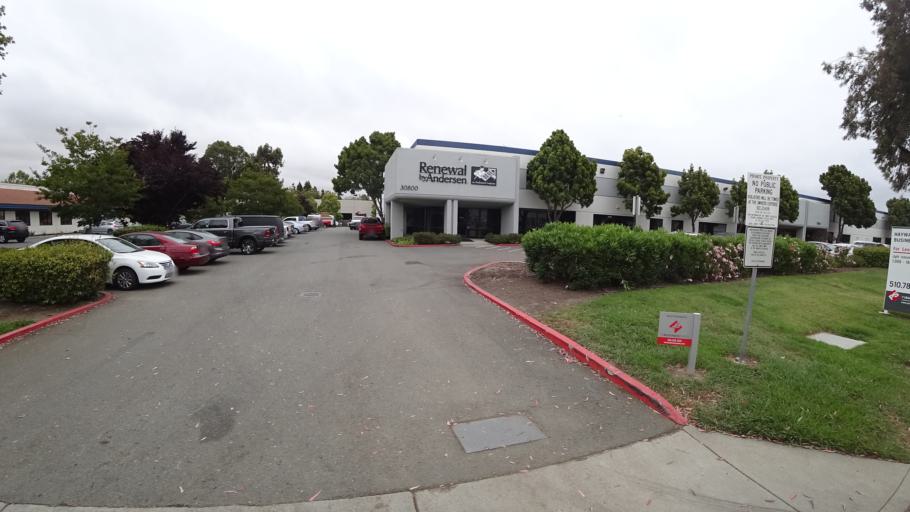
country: US
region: California
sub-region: Alameda County
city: Union City
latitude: 37.6161
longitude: -122.0572
